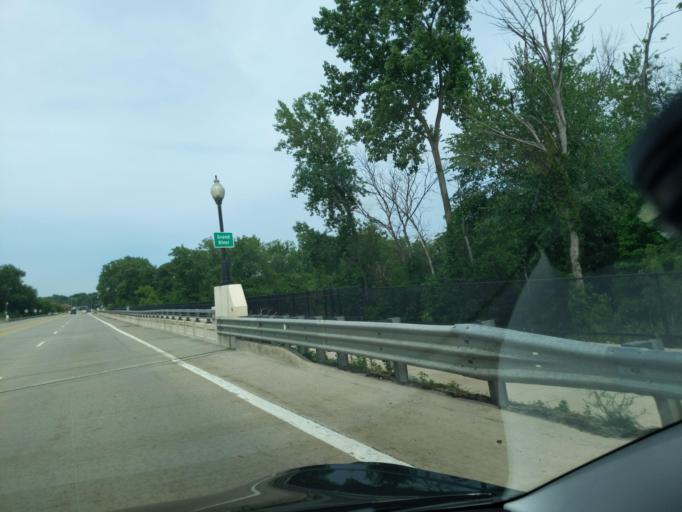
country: US
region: Michigan
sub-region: Kent County
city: Forest Hills
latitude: 42.9554
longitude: -85.4743
